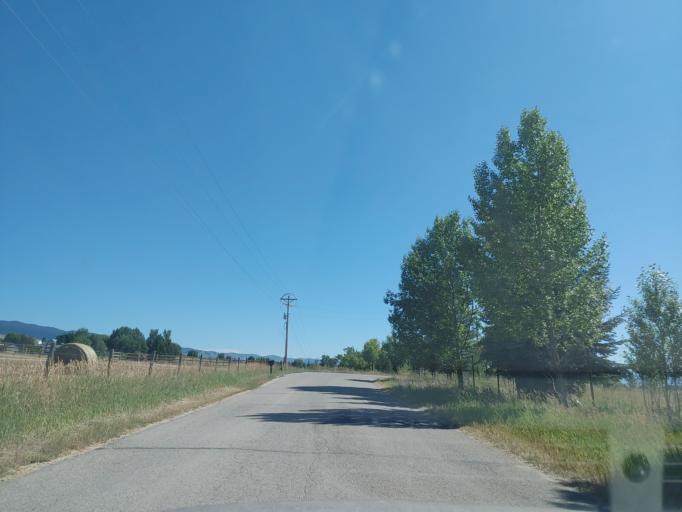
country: US
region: Montana
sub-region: Ravalli County
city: Hamilton
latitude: 46.3462
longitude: -114.0615
